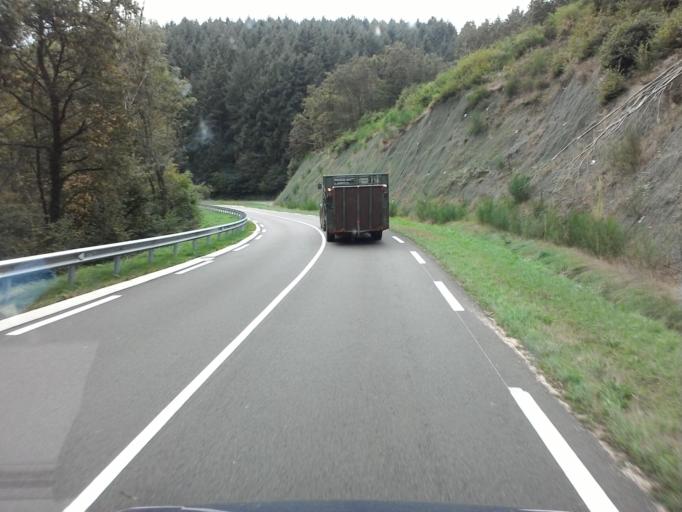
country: FR
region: Bourgogne
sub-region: Departement de Saone-et-Loire
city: Saint-Eusebe
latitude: 46.5963
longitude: 4.5001
